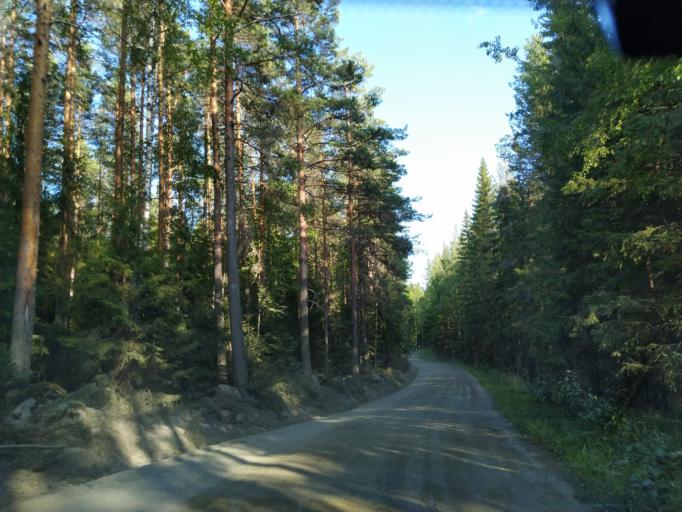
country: FI
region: Central Finland
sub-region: Jaemsae
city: Kuhmoinen
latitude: 61.6761
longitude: 24.9951
